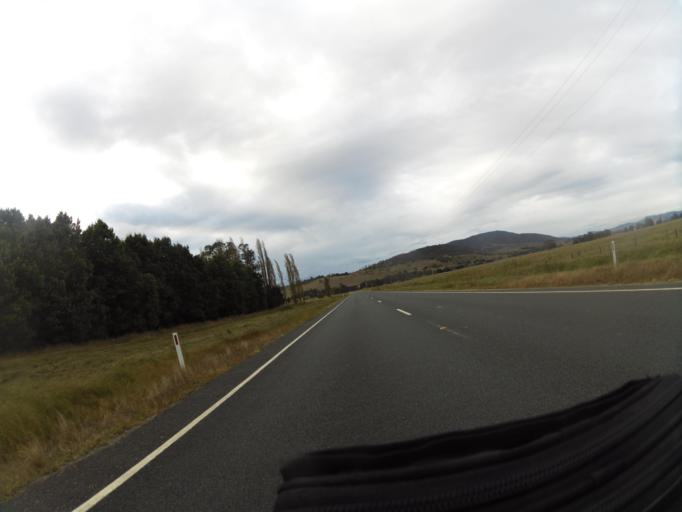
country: AU
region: New South Wales
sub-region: Snowy River
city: Jindabyne
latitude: -36.1167
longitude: 147.9798
